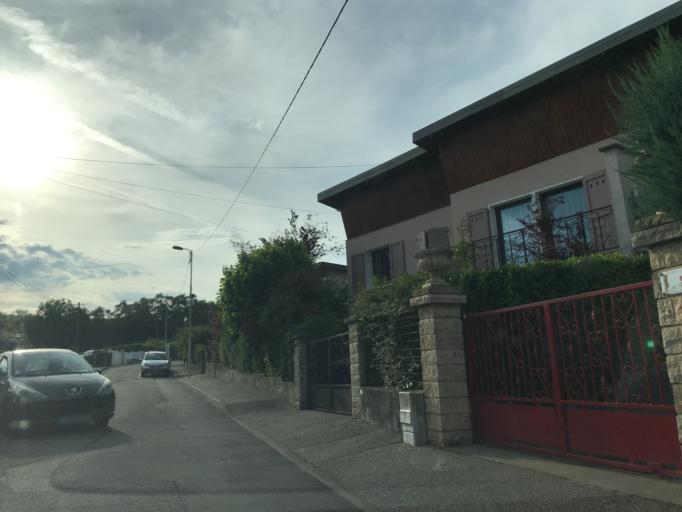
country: FR
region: Rhone-Alpes
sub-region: Departement de la Savoie
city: Cognin
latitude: 45.5647
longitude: 5.9053
